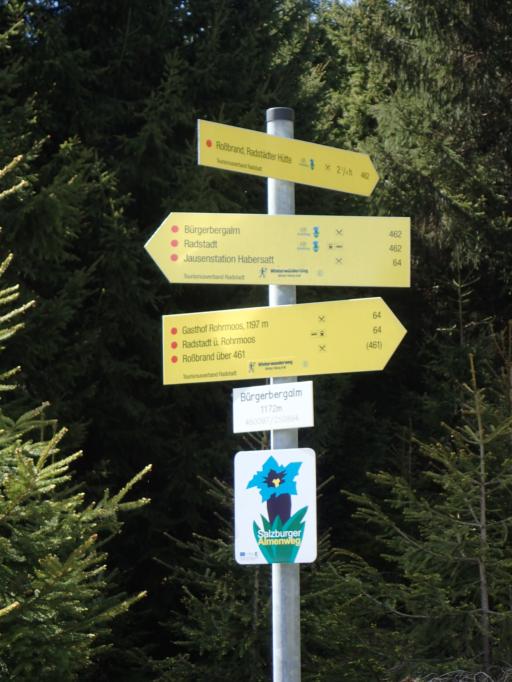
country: AT
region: Salzburg
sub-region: Politischer Bezirk Sankt Johann im Pongau
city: Radstadt
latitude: 47.3966
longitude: 13.4662
